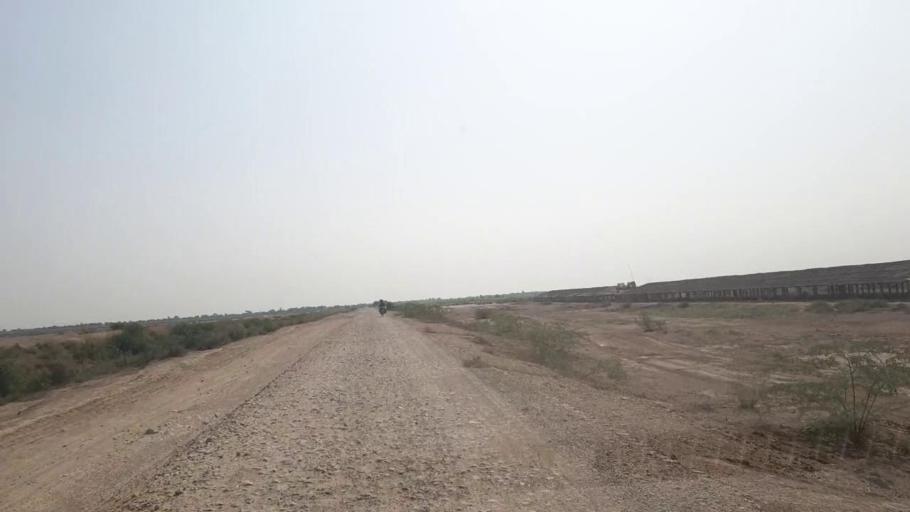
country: PK
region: Sindh
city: Kadhan
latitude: 24.4767
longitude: 68.9022
